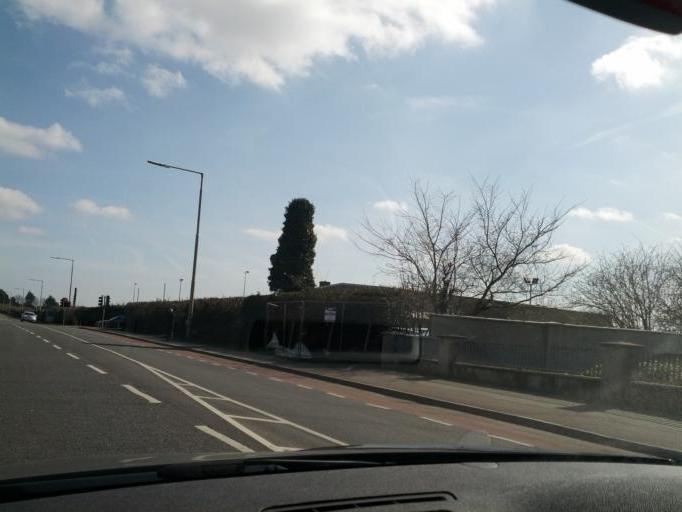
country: IE
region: Leinster
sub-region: Kildare
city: Leixlip
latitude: 53.3715
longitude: -6.5148
